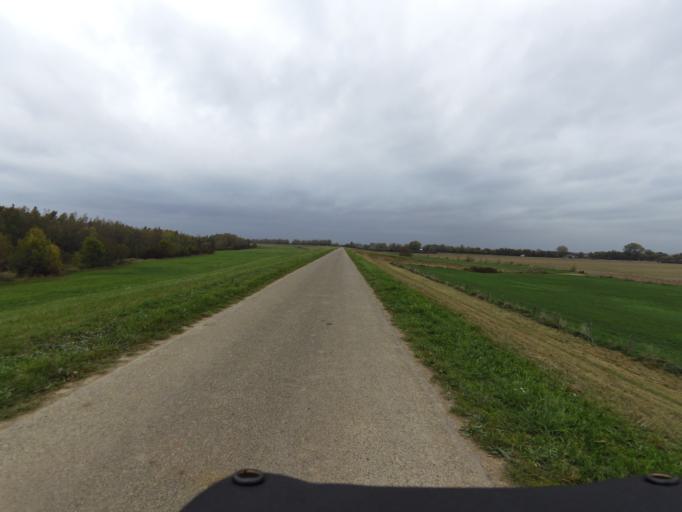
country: NL
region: Gelderland
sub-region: Gemeente Zevenaar
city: Zevenaar
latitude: 51.8683
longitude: 6.1003
